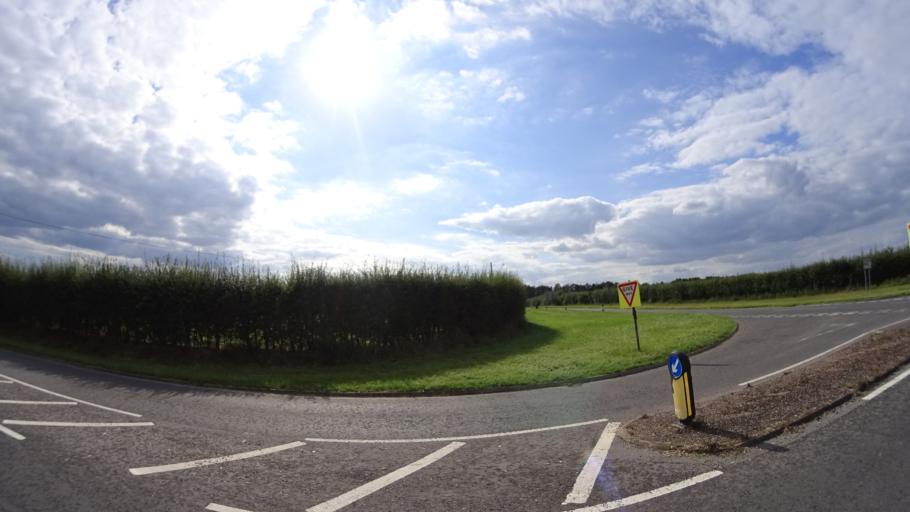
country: GB
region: England
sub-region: Hampshire
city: East Dean
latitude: 51.1121
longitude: -1.5778
